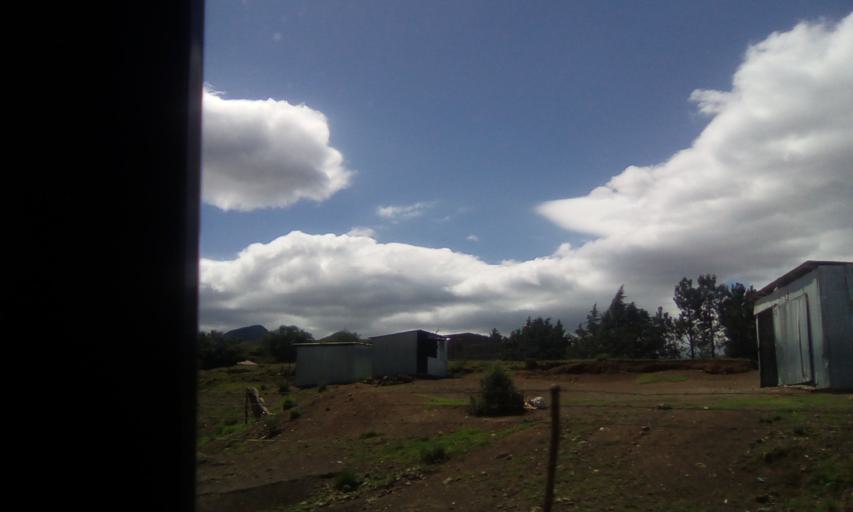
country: LS
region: Maseru
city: Nako
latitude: -29.6608
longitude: 27.8067
